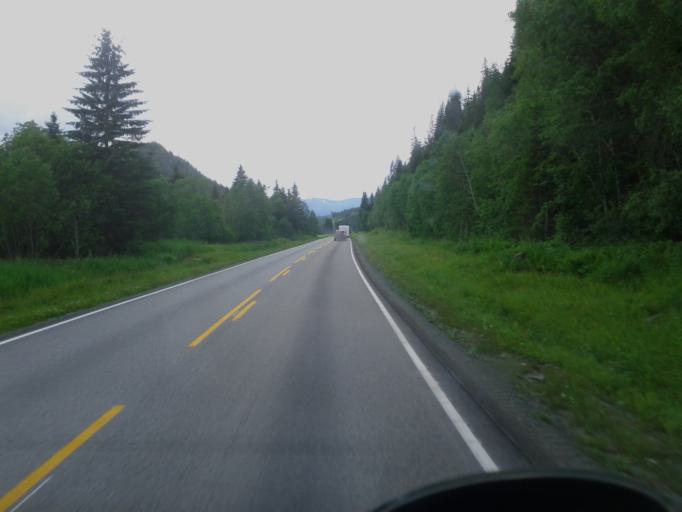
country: NO
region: Nord-Trondelag
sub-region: Grong
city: Grong
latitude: 64.5171
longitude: 12.3755
